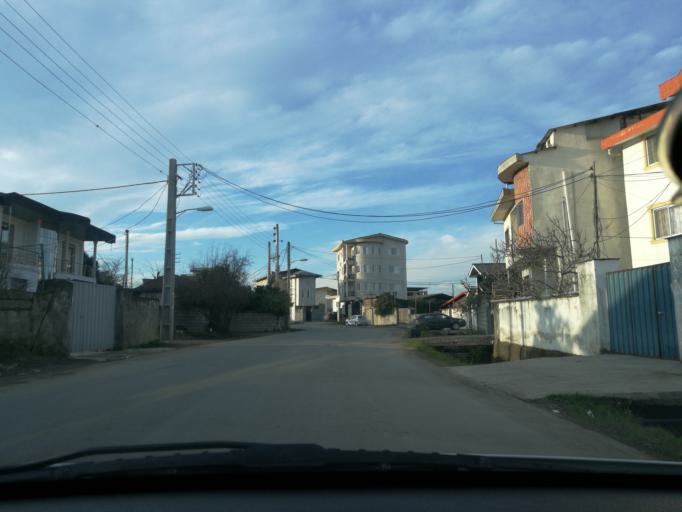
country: IR
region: Mazandaran
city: Chalus
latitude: 36.6441
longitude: 51.4336
